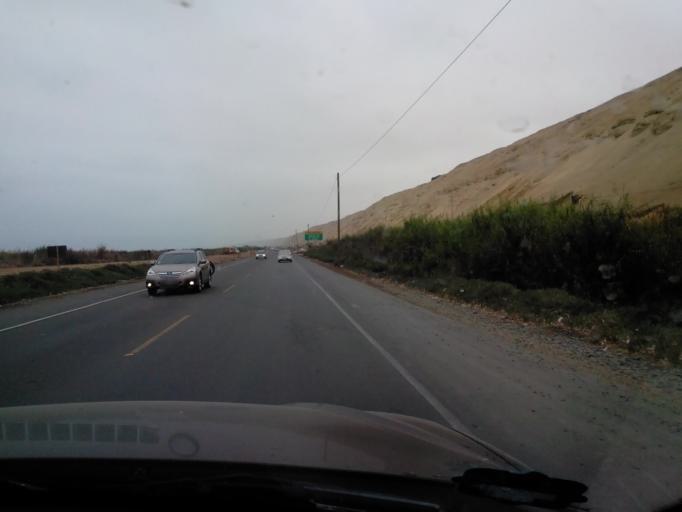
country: PE
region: Ica
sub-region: Provincia de Chincha
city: San Pedro
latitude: -13.4066
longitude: -76.1922
